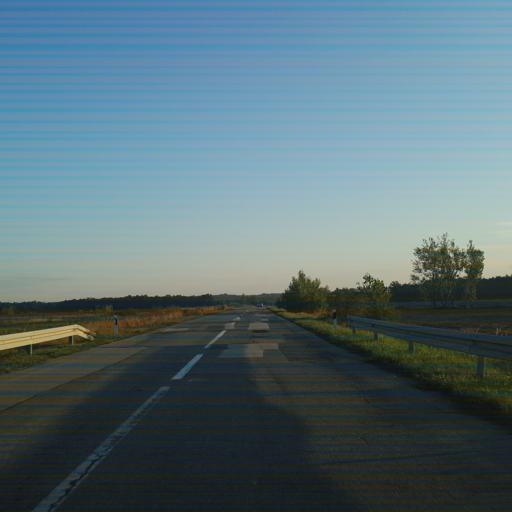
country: RS
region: Central Serbia
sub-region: Borski Okrug
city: Negotin
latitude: 44.1387
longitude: 22.3484
